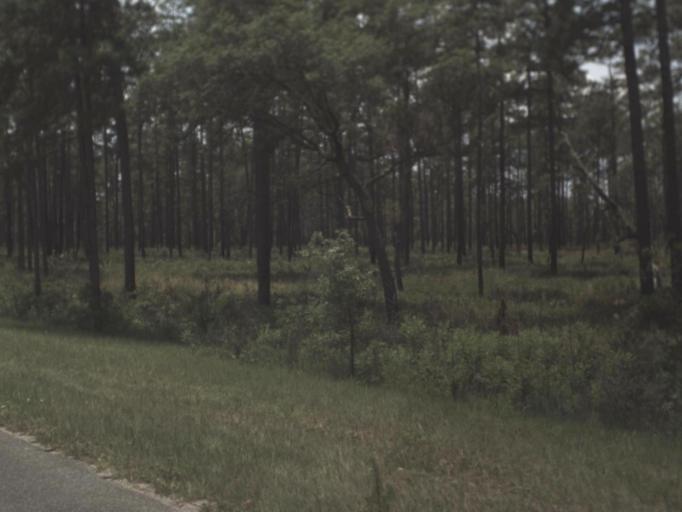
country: US
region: Florida
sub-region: Putnam County
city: Crescent City
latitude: 29.4145
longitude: -81.7371
